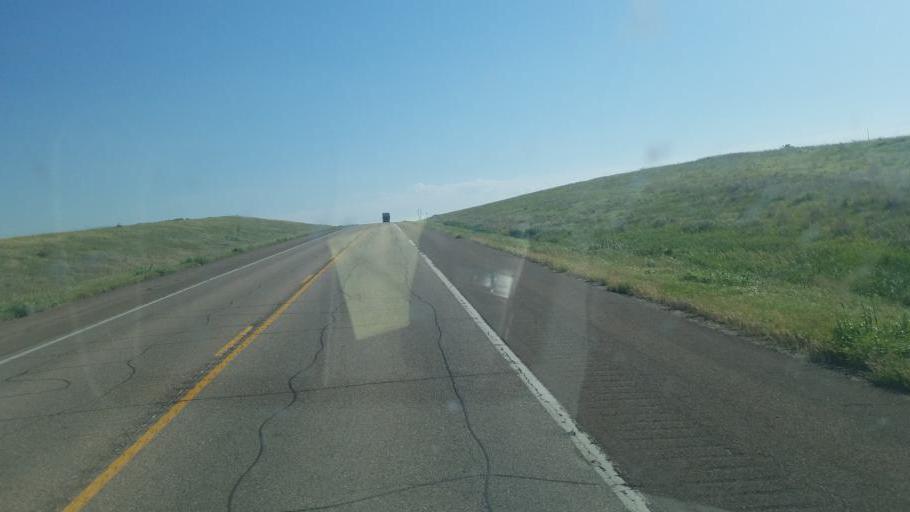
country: US
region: Kansas
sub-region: Barton County
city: Great Bend
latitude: 38.3840
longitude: -98.6817
